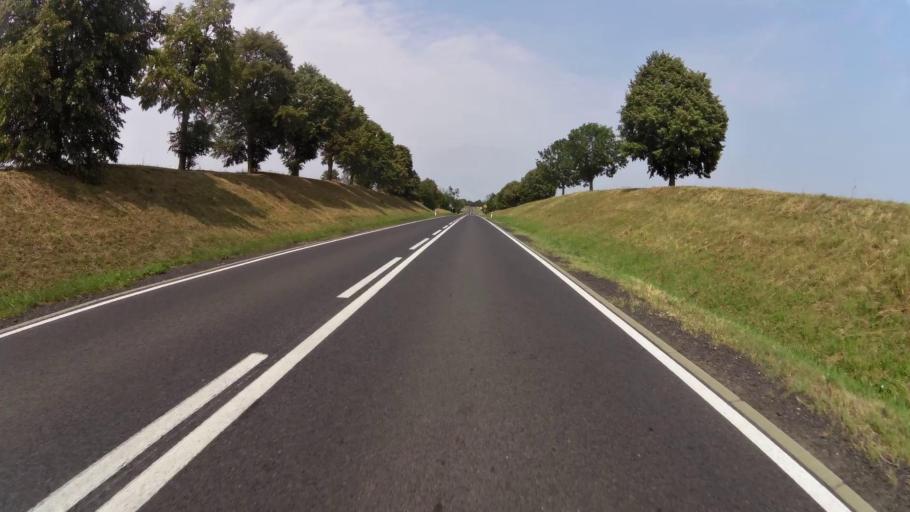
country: PL
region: West Pomeranian Voivodeship
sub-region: Powiat gryfinski
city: Mieszkowice
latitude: 52.8417
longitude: 14.4928
